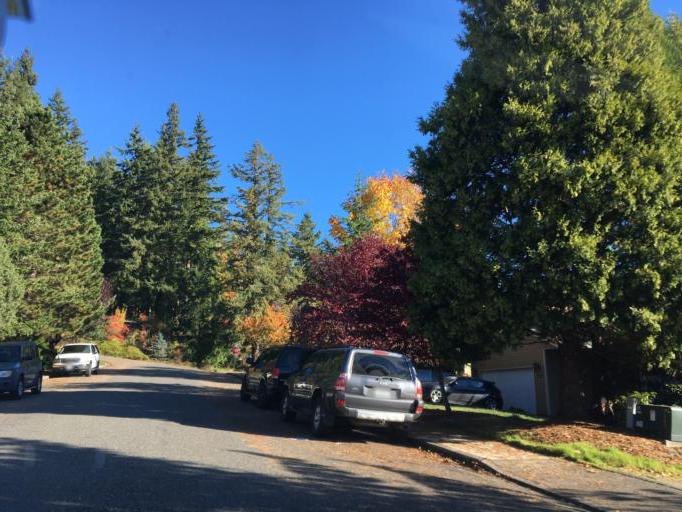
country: US
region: Washington
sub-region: Whatcom County
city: Geneva
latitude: 48.7683
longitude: -122.4239
